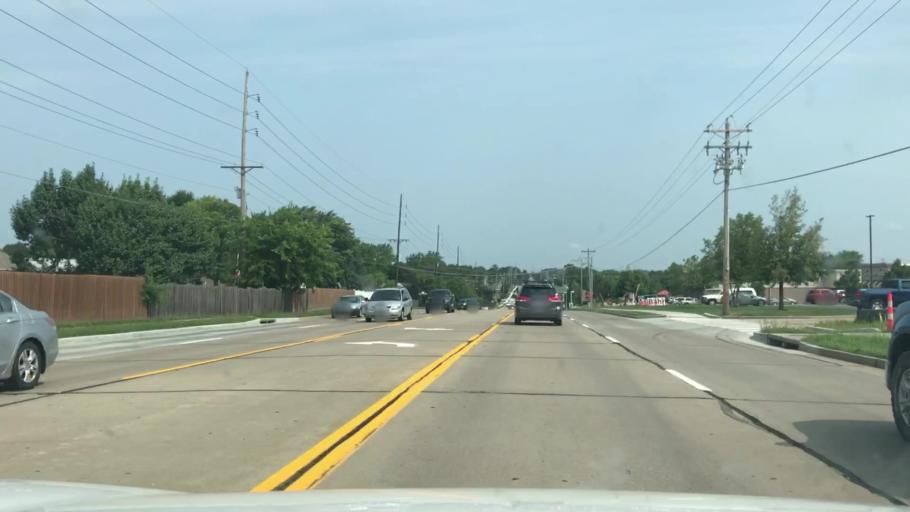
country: US
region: Missouri
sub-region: Saint Charles County
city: Dardenne Prairie
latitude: 38.7855
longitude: -90.7370
